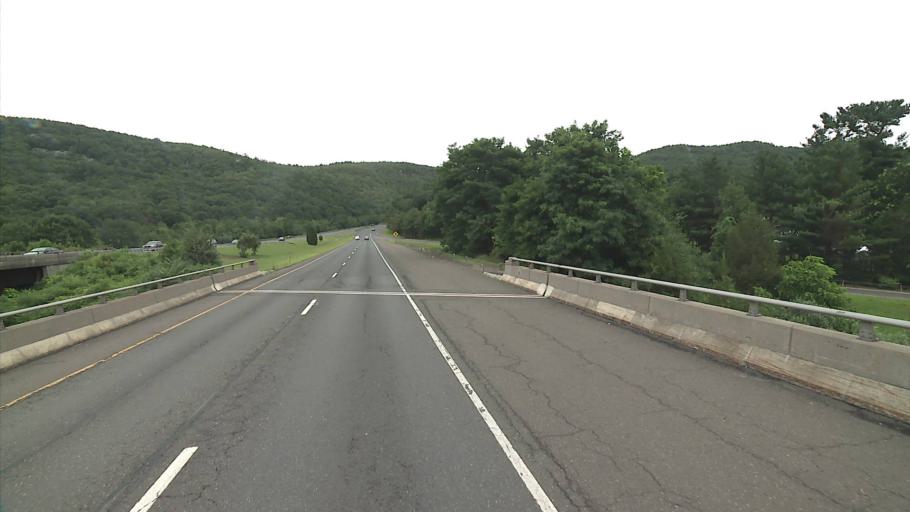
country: US
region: Connecticut
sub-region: New Haven County
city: Naugatuck
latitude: 41.4444
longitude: -73.0668
